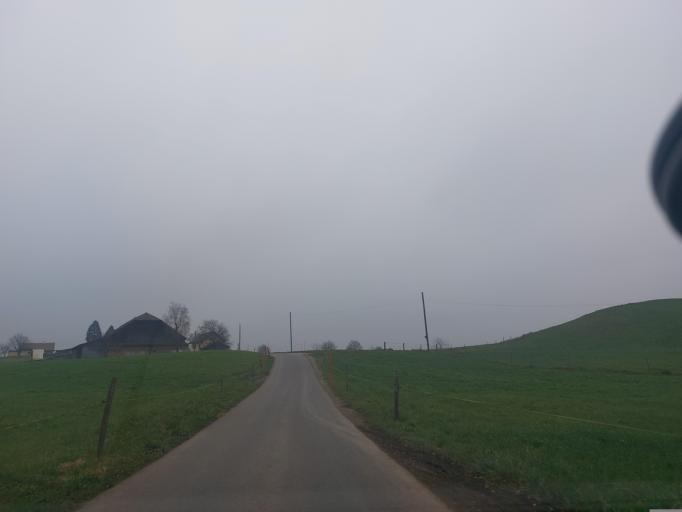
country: CH
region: Vaud
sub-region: Lavaux-Oron District
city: Palezieux
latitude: 46.5611
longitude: 6.8585
